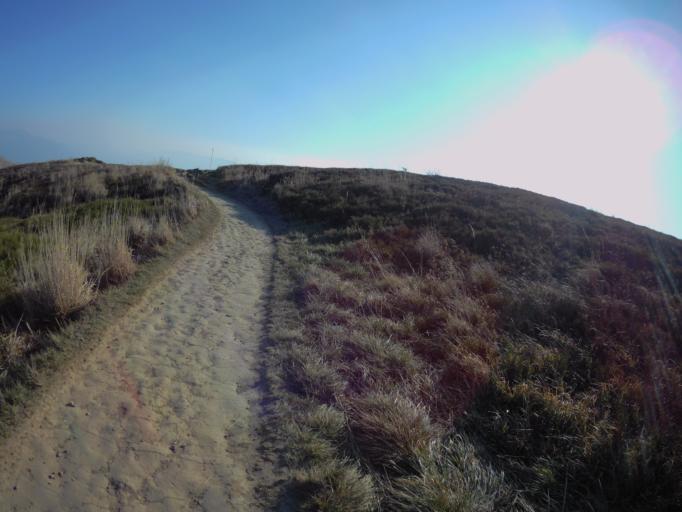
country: PL
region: Subcarpathian Voivodeship
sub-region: Powiat bieszczadzki
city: Lutowiska
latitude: 49.1368
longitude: 22.6059
